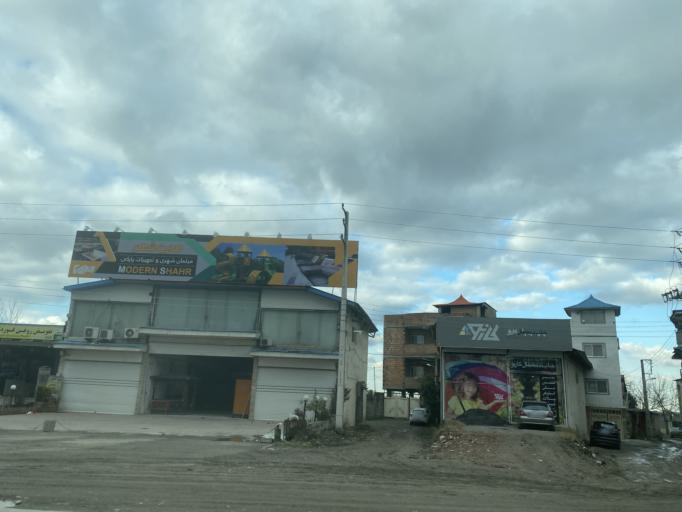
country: IR
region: Mazandaran
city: Amol
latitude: 36.4333
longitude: 52.3553
